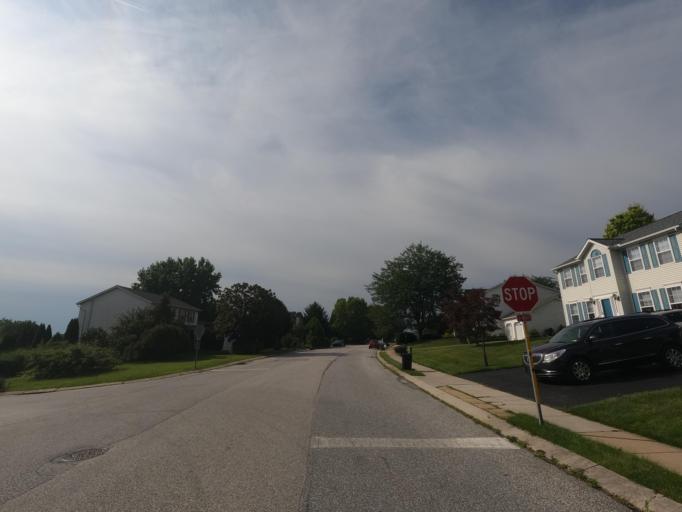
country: US
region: Pennsylvania
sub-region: York County
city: Stewartstown
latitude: 39.7623
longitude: -76.5868
